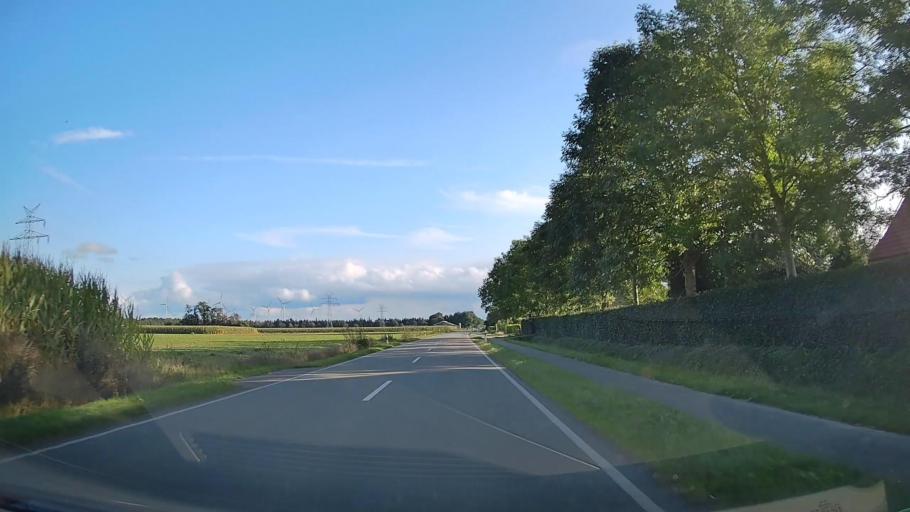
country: DE
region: Lower Saxony
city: Barssel
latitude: 53.1072
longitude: 7.7081
